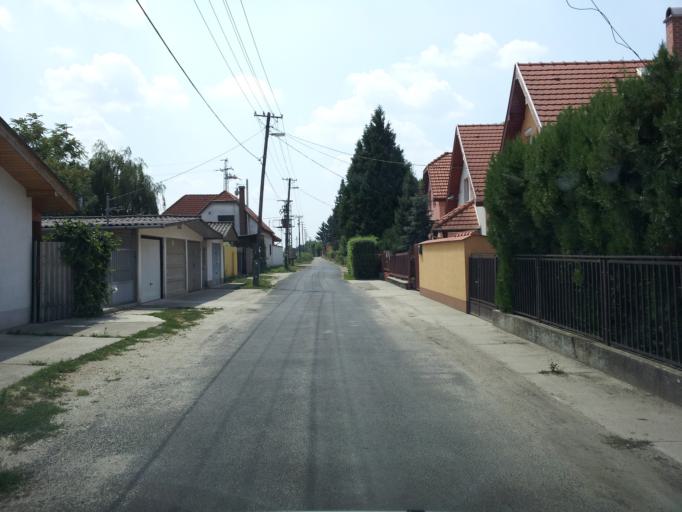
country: HU
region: Pest
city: Szigethalom
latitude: 47.2968
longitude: 19.0252
